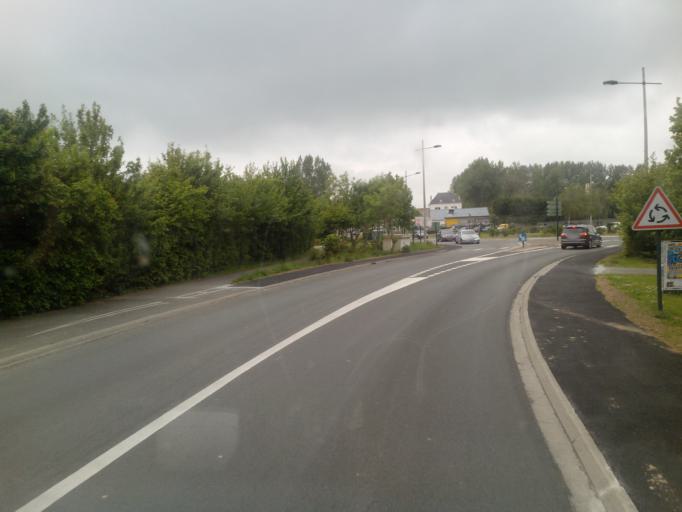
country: FR
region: Nord-Pas-de-Calais
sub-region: Departement du Pas-de-Calais
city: Condette
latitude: 50.6516
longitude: 1.6424
